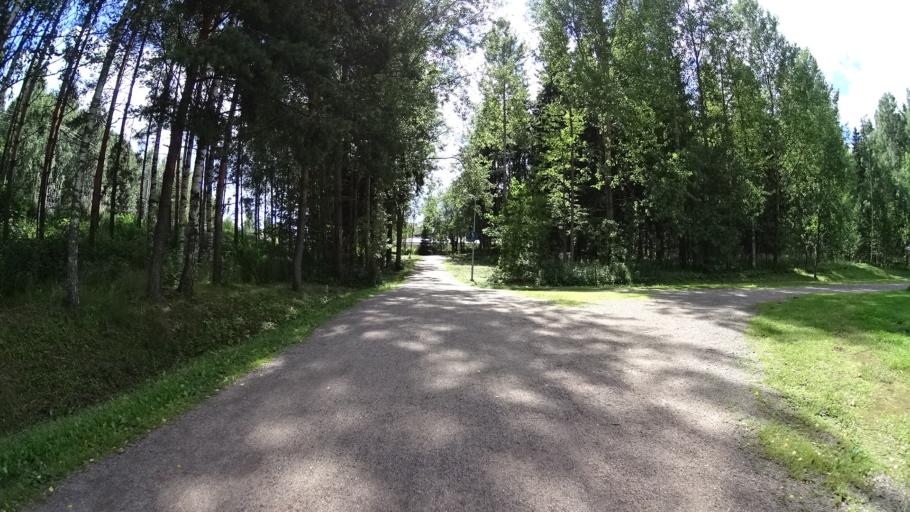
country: FI
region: Uusimaa
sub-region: Helsinki
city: Teekkarikylae
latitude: 60.2735
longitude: 24.8515
